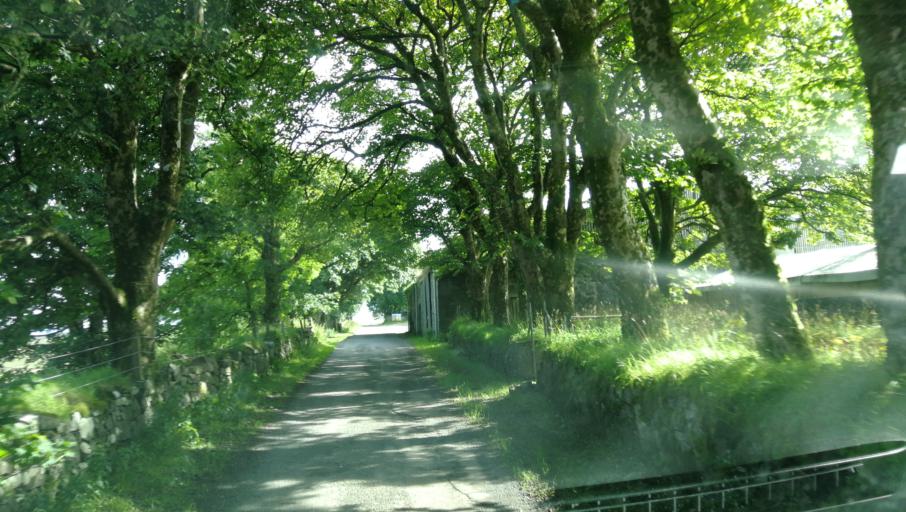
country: GB
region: Scotland
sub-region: Highland
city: Isle of Skye
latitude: 57.3967
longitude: -6.5674
